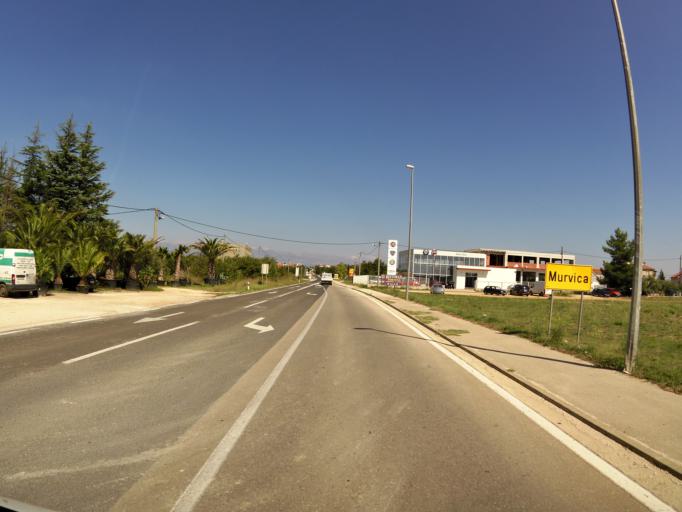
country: HR
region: Zadarska
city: Policnik
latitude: 44.1408
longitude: 15.3138
